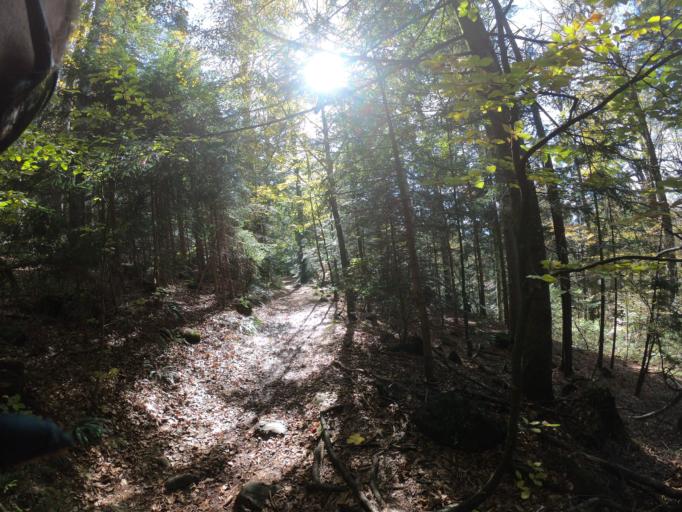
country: DE
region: Bavaria
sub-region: Lower Bavaria
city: Bodenmais
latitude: 49.0843
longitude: 13.1143
